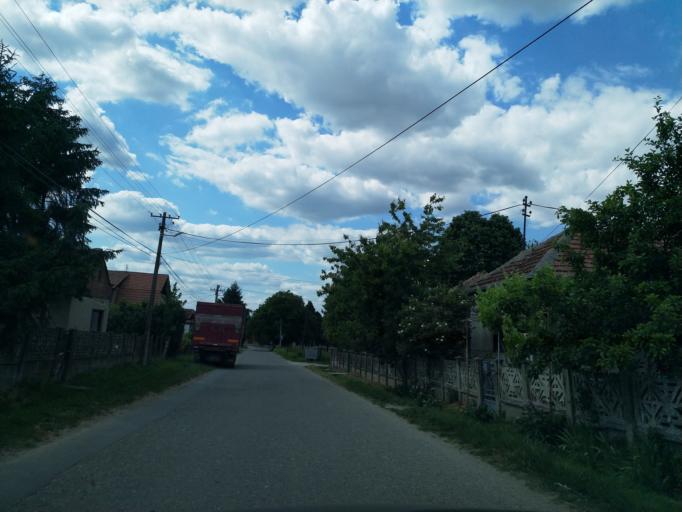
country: RS
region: Central Serbia
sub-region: Pomoravski Okrug
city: Jagodina
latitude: 43.9432
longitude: 21.2983
